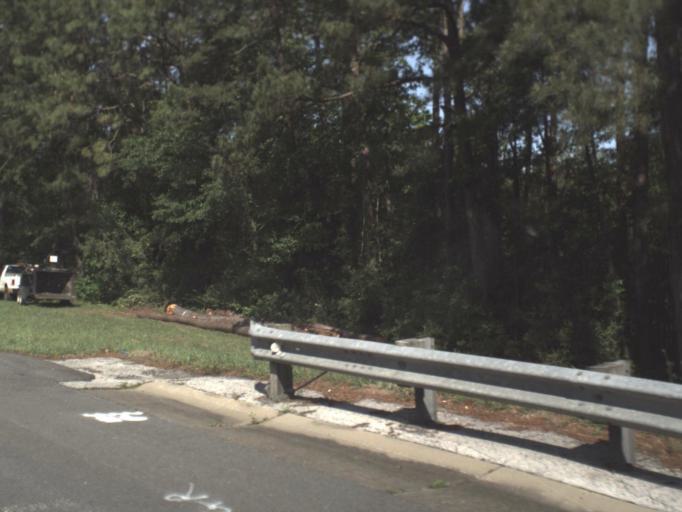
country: US
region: Florida
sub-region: Walton County
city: DeFuniak Springs
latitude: 30.7069
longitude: -85.9515
